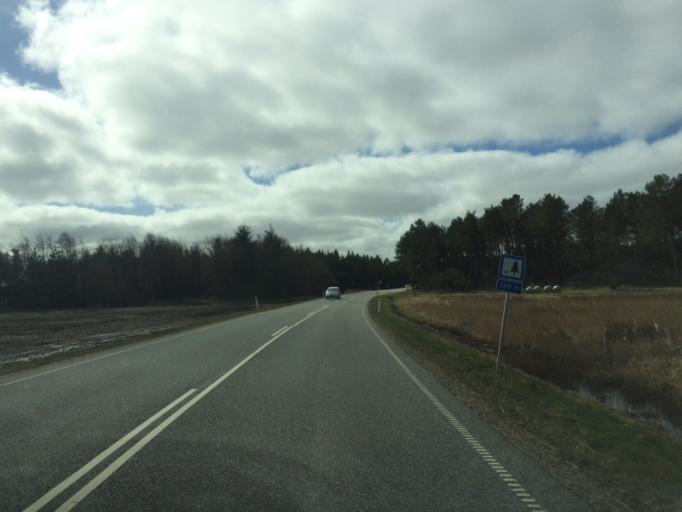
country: DK
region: Central Jutland
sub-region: Holstebro Kommune
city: Ulfborg
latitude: 56.2904
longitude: 8.1858
